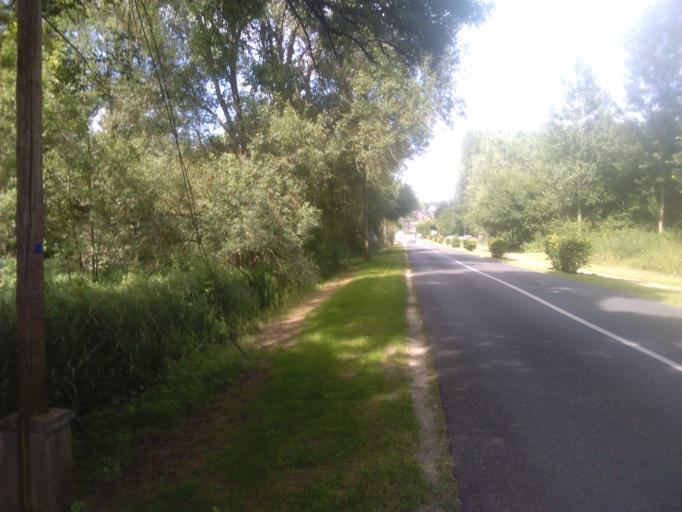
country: FR
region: Centre
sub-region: Departement du Loir-et-Cher
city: Chouzy-sur-Cisse
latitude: 47.5600
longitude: 1.2102
